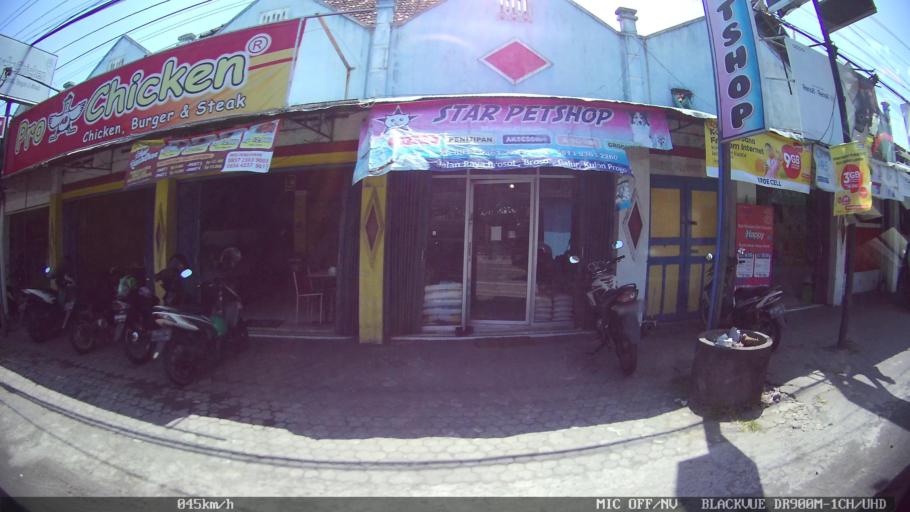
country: ID
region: Daerah Istimewa Yogyakarta
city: Srandakan
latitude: -7.9402
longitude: 110.2351
